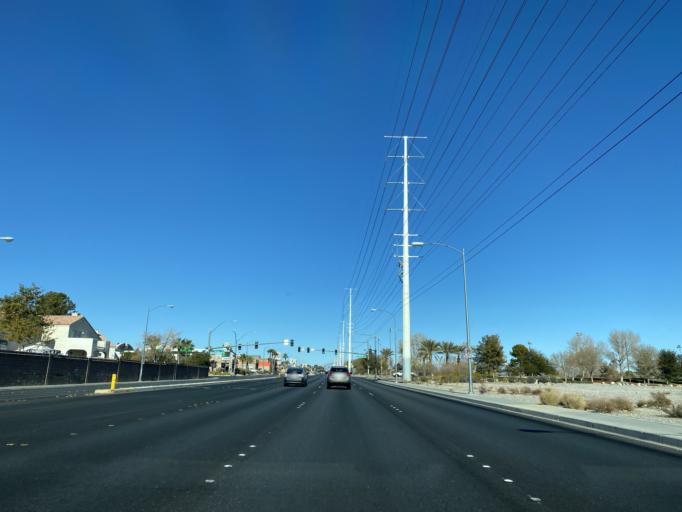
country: US
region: Nevada
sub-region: Clark County
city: Spring Valley
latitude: 36.1210
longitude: -115.2789
